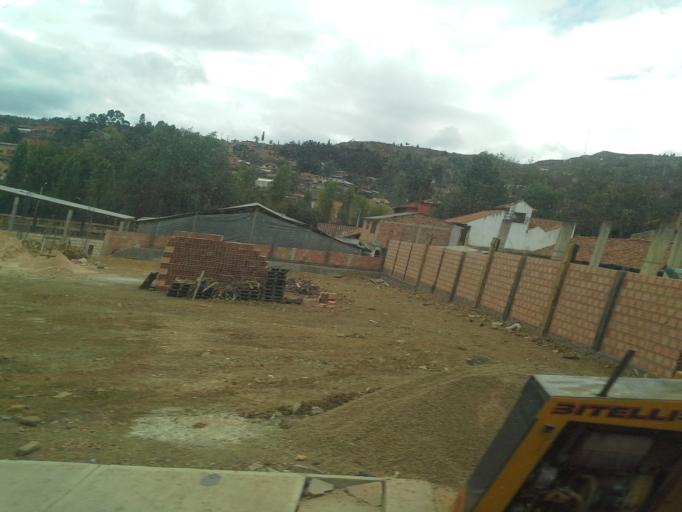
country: CO
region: Boyaca
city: Raquira
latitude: 5.5384
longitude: -73.6344
